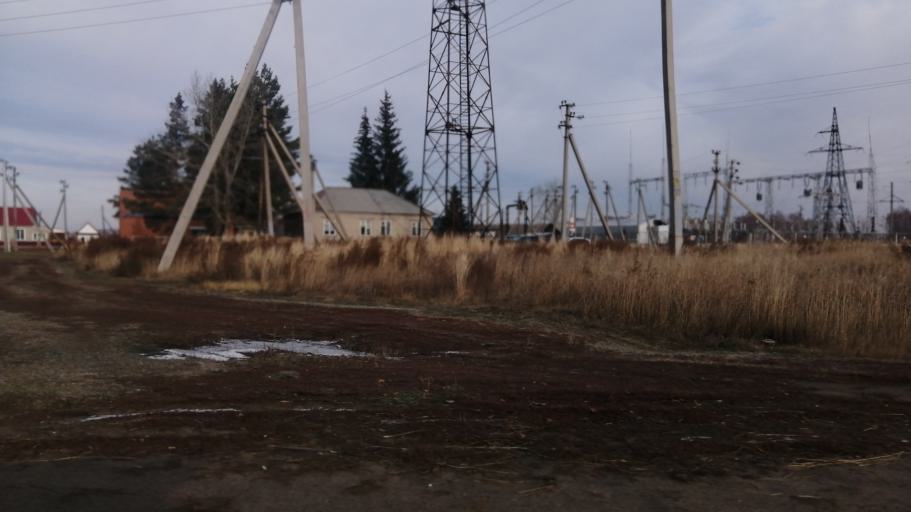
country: RU
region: Novosibirsk
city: Krasnozerskoye
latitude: 53.9887
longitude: 78.7266
